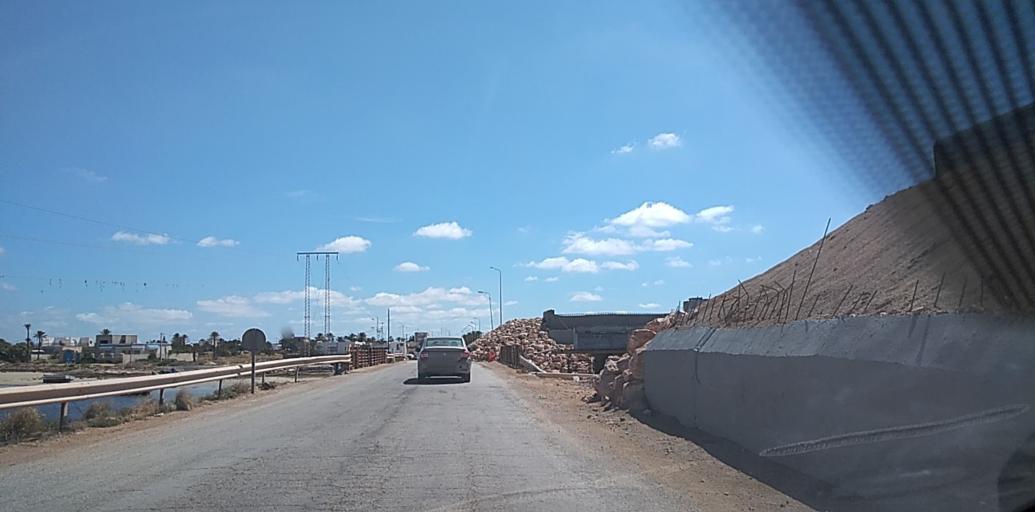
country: TN
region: Safaqis
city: Al Qarmadah
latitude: 34.6629
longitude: 11.1244
